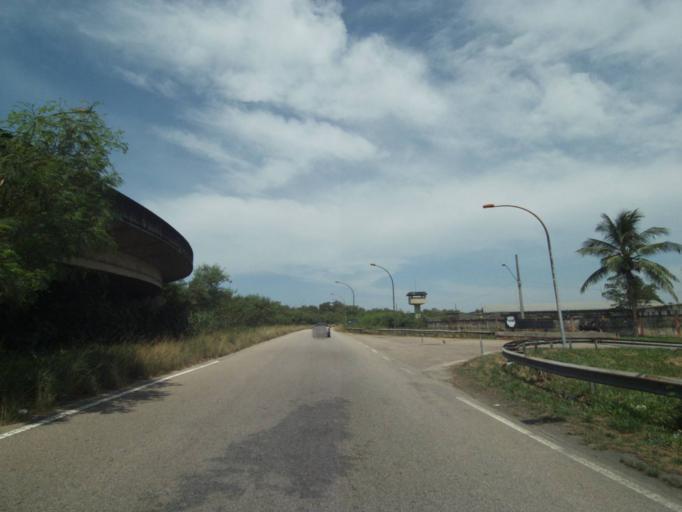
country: BR
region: Rio de Janeiro
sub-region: Duque De Caxias
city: Duque de Caxias
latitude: -22.8068
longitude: -43.2902
